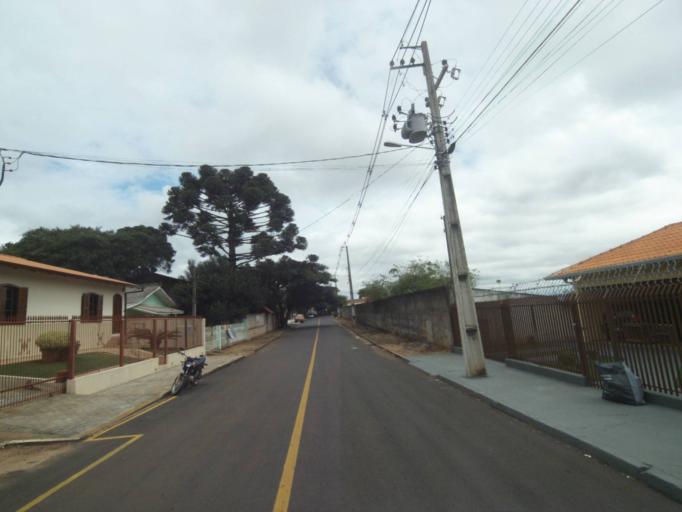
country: BR
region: Parana
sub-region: Telemaco Borba
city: Telemaco Borba
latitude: -24.3358
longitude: -50.6252
